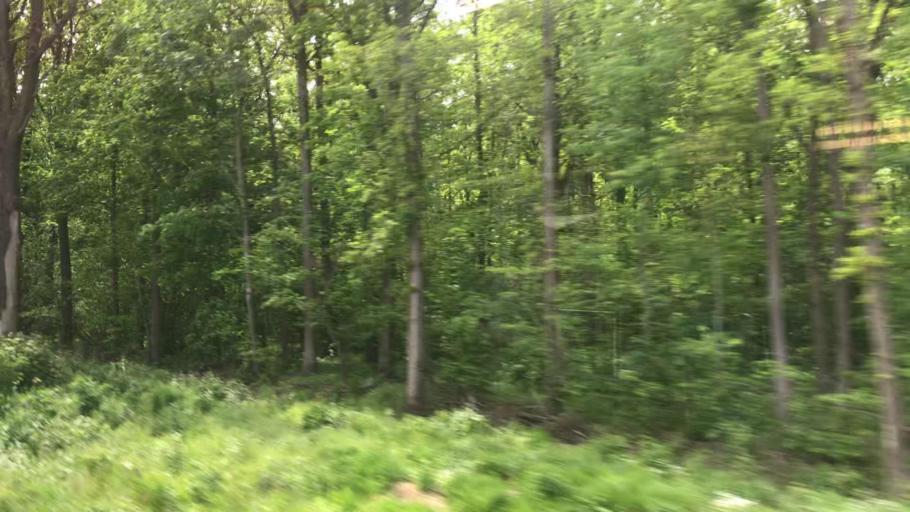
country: PL
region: Lower Silesian Voivodeship
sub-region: Powiat wroclawski
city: Katy Wroclawskie
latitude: 51.0023
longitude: 16.6916
